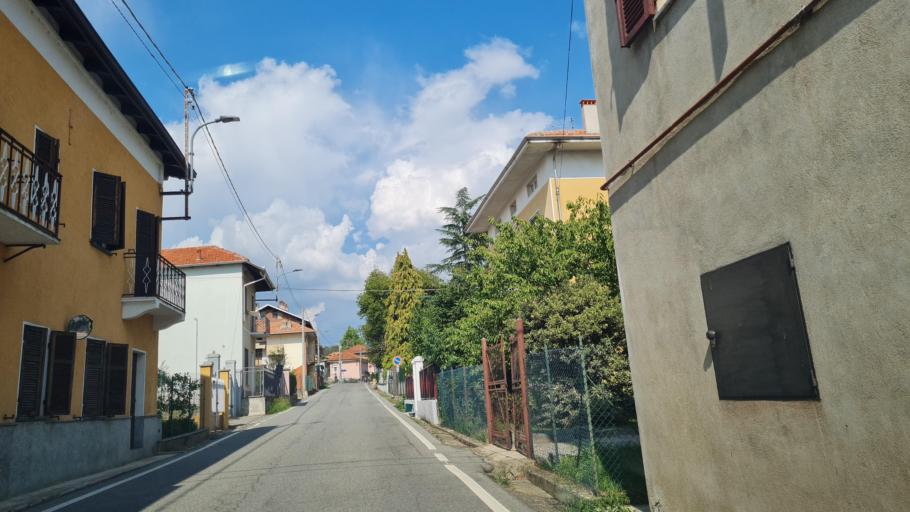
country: IT
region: Piedmont
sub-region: Provincia di Biella
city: Cossato
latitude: 45.5773
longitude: 8.1807
